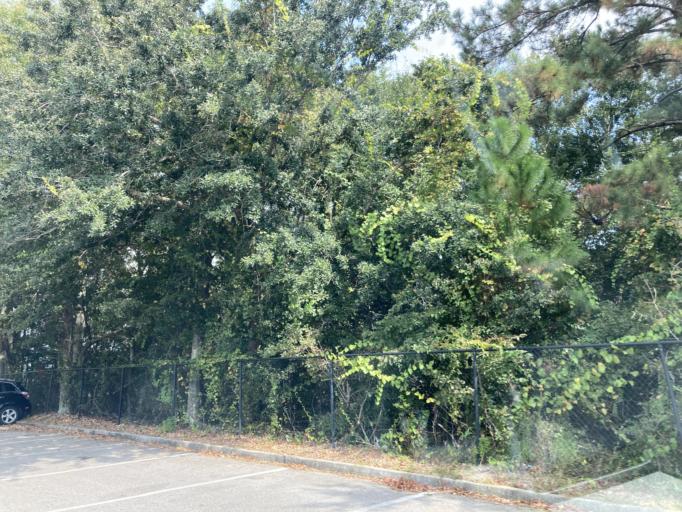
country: US
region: Mississippi
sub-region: Jackson County
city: Gulf Hills
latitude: 30.4510
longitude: -88.8435
